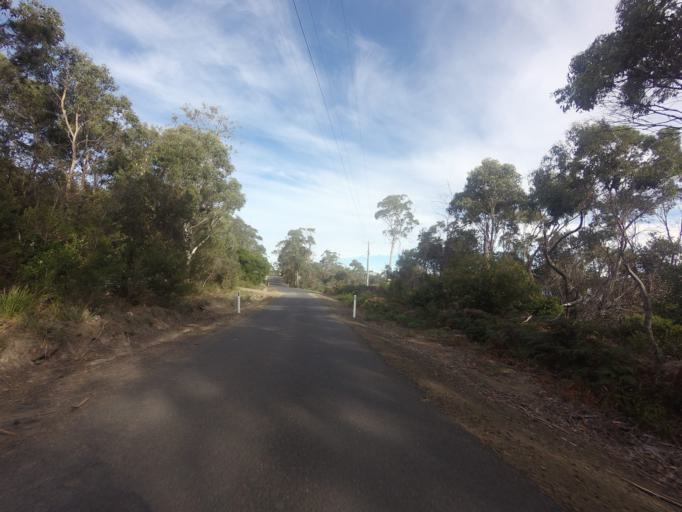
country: AU
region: Tasmania
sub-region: Sorell
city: Sorell
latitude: -42.9754
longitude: 147.8367
